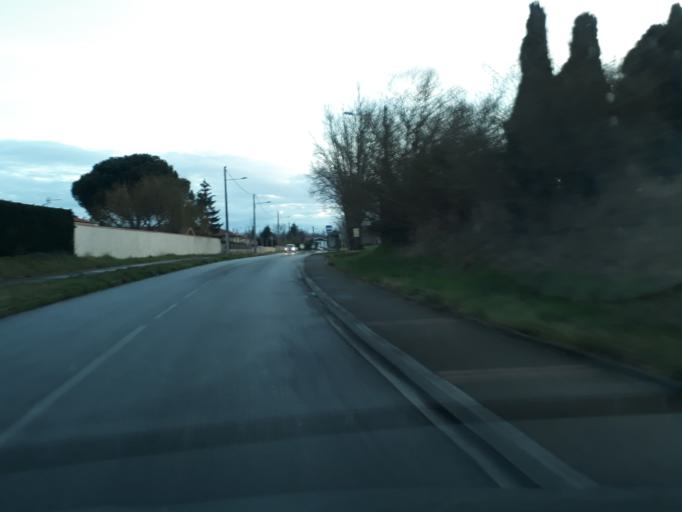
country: FR
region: Midi-Pyrenees
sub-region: Departement de la Haute-Garonne
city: Marquefave
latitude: 43.3172
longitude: 1.2411
